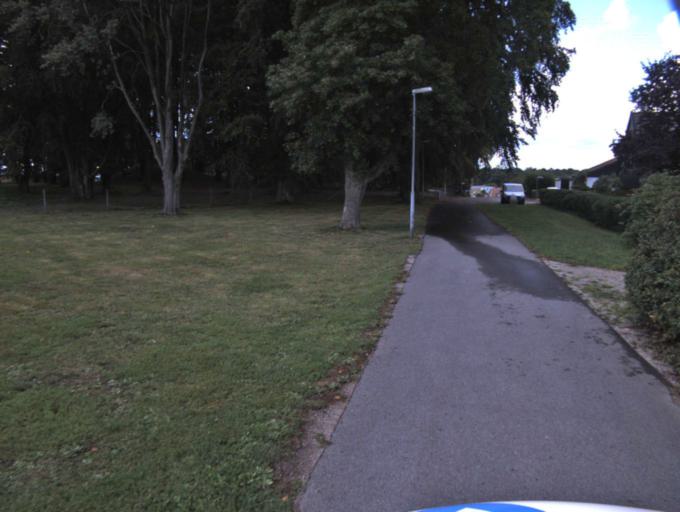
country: SE
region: Skane
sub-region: Kavlinge Kommun
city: Kaevlinge
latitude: 55.7719
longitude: 13.0967
